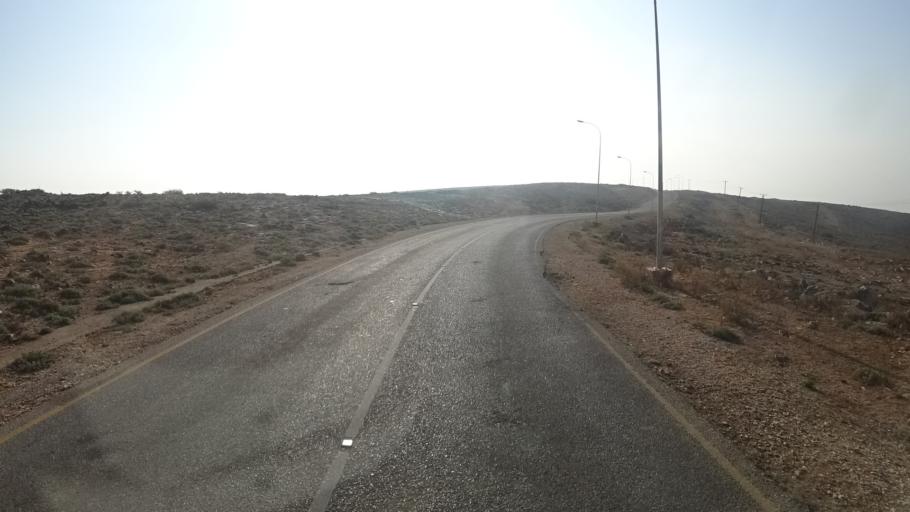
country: YE
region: Al Mahrah
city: Hawf
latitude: 16.7660
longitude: 53.2314
